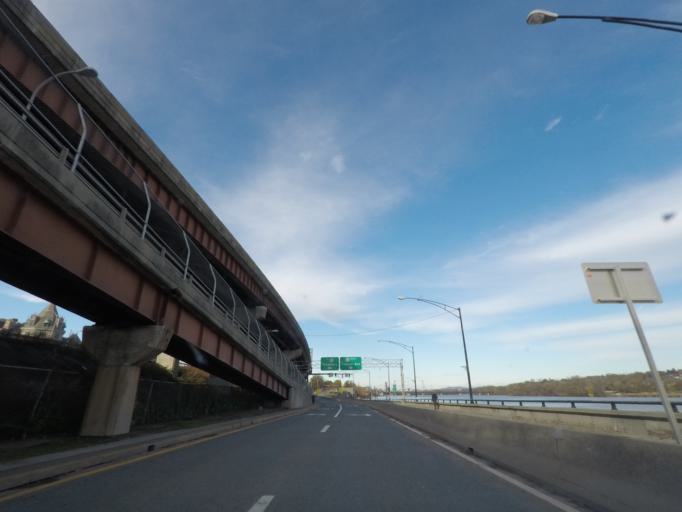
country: US
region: New York
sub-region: Rensselaer County
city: Rensselaer
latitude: 42.6453
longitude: -73.7487
